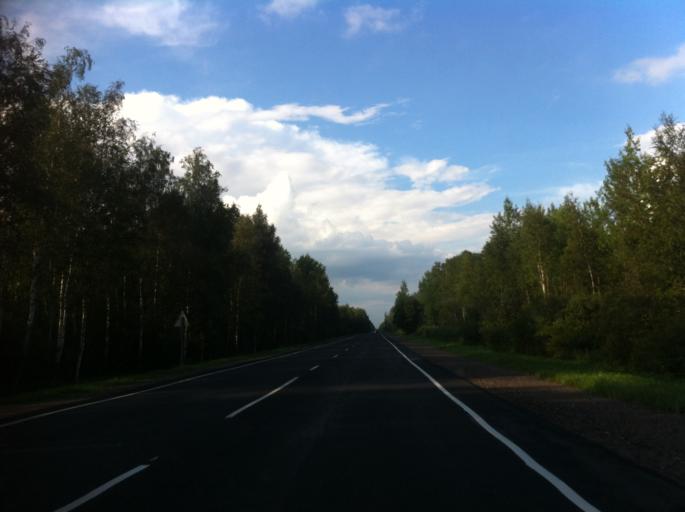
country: RU
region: Leningrad
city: Luga
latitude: 58.4688
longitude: 29.7685
